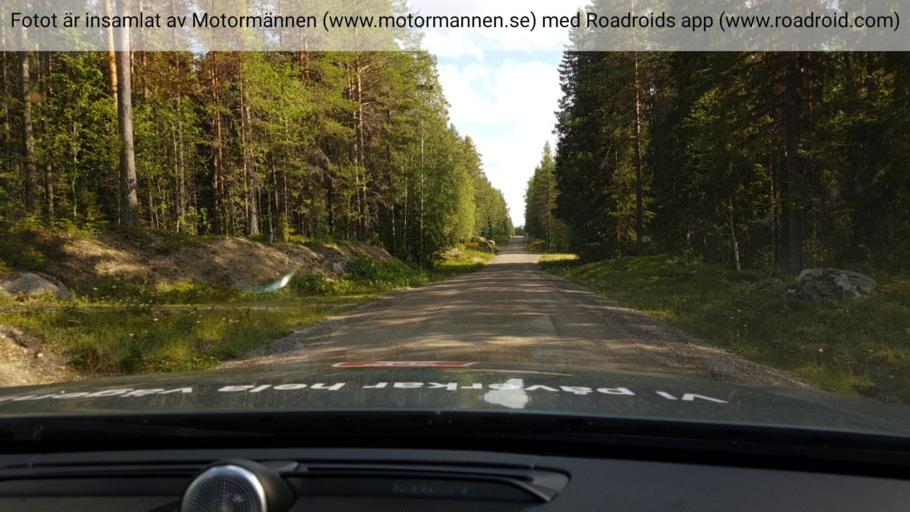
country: SE
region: Vaesterbotten
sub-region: Dorotea Kommun
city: Dorotea
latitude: 63.9611
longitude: 16.0744
